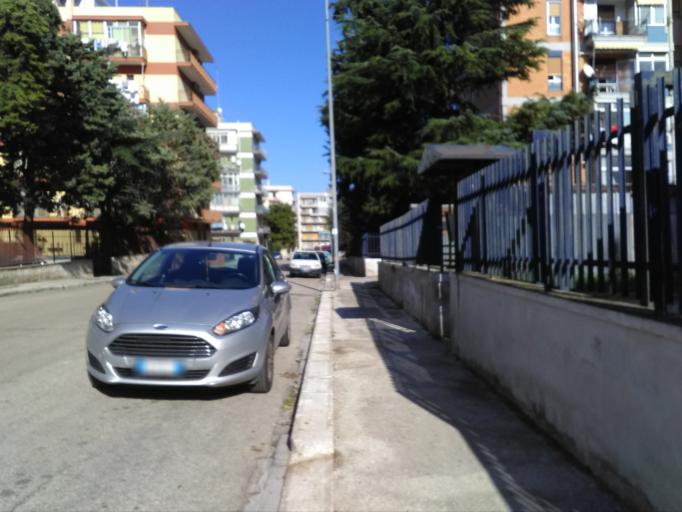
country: IT
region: Apulia
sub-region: Provincia di Bari
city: Bari
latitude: 41.1107
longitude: 16.8920
